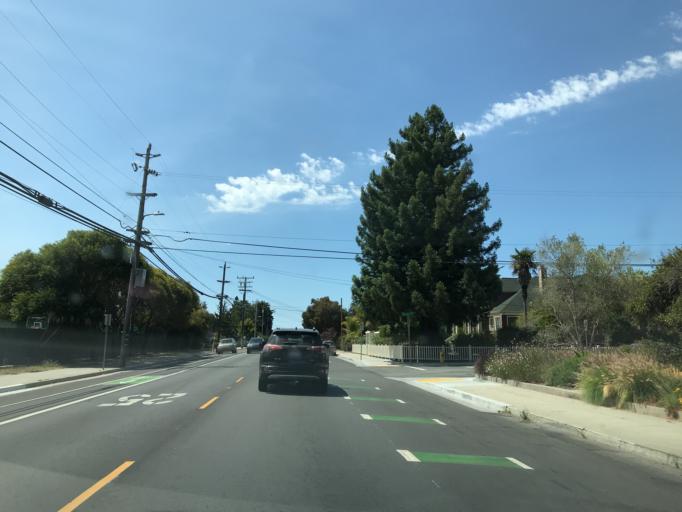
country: US
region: California
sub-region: Santa Cruz County
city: Santa Cruz
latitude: 36.9665
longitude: -122.0352
